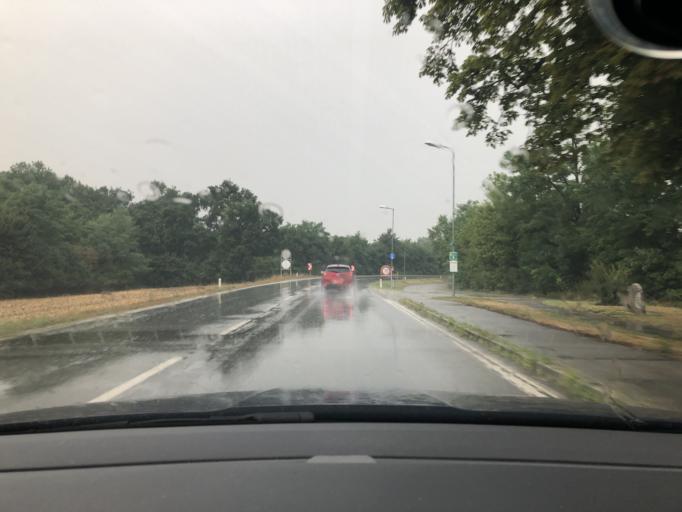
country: AT
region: Lower Austria
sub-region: Politischer Bezirk Ganserndorf
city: Marchegg
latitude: 48.2691
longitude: 16.9066
